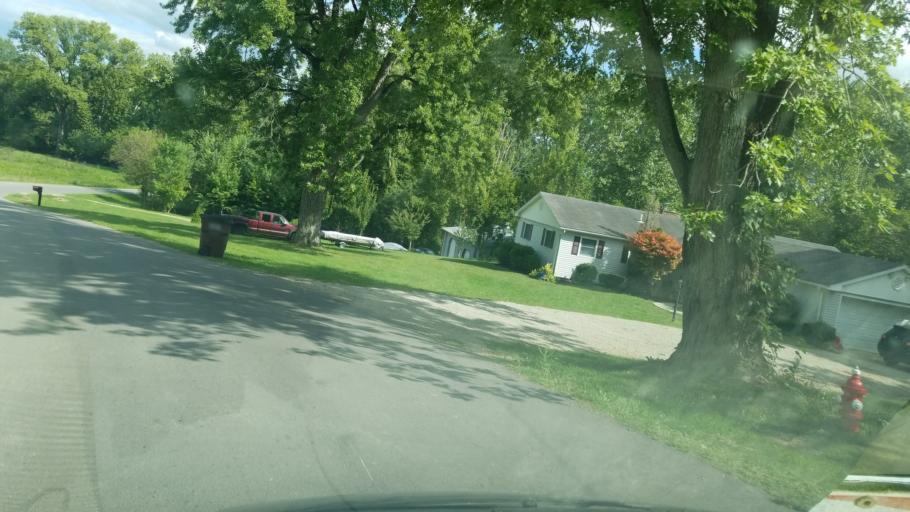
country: US
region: Ohio
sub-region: Logan County
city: De Graff
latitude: 40.3089
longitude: -83.9216
